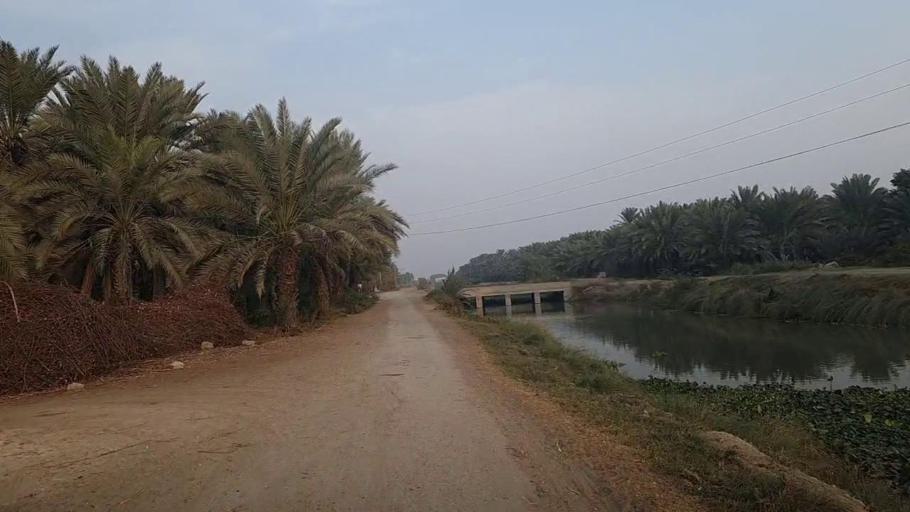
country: PK
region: Sindh
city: Kot Diji
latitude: 27.3581
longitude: 68.6519
